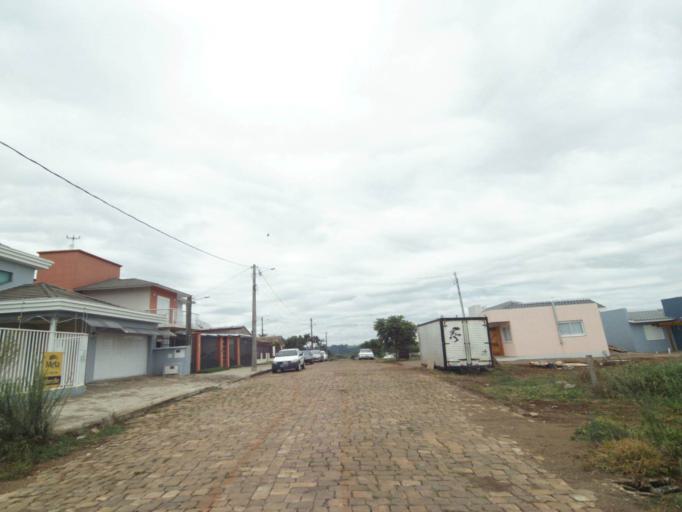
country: BR
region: Rio Grande do Sul
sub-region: Lagoa Vermelha
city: Lagoa Vermelha
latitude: -28.2171
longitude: -51.5332
